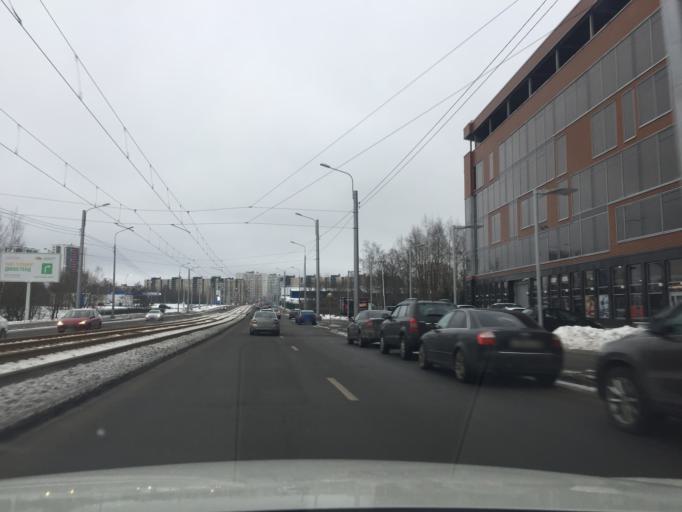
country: RU
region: St.-Petersburg
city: Krasnogvargeisky
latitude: 59.9624
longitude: 30.4666
